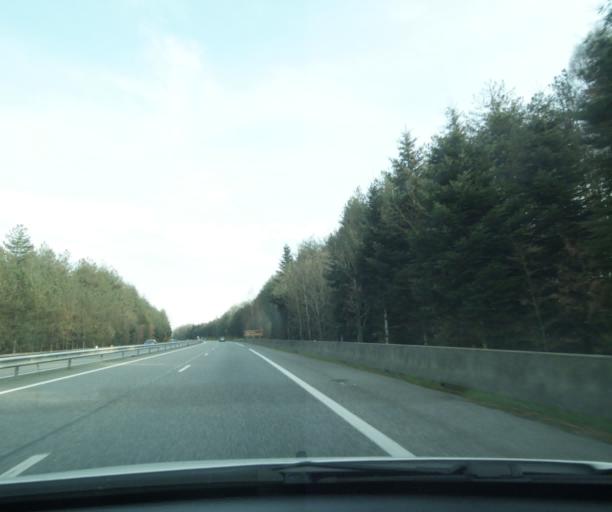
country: FR
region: Midi-Pyrenees
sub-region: Departement de la Haute-Garonne
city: Montrejeau
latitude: 43.0933
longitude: 0.5037
